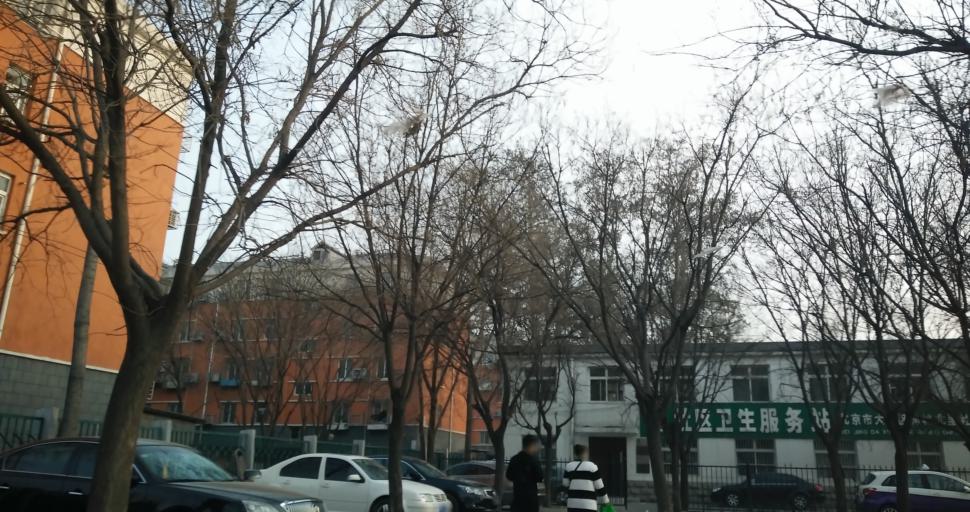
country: CN
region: Beijing
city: Xingfeng
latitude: 39.7228
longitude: 116.3340
